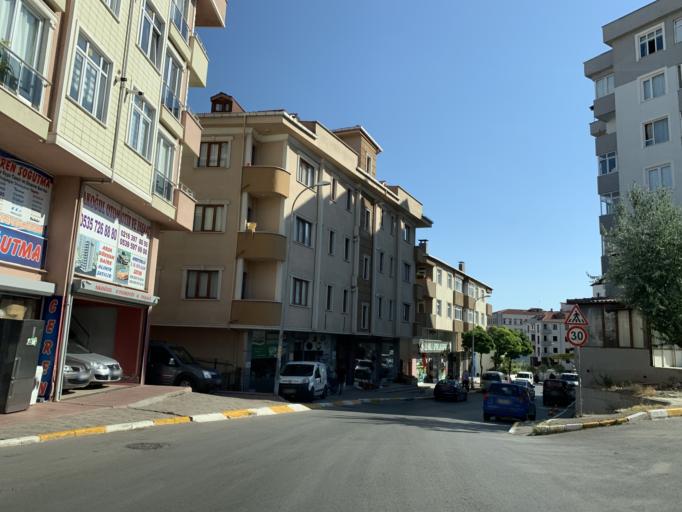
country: TR
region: Istanbul
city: Pendik
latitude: 40.8818
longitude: 29.2678
